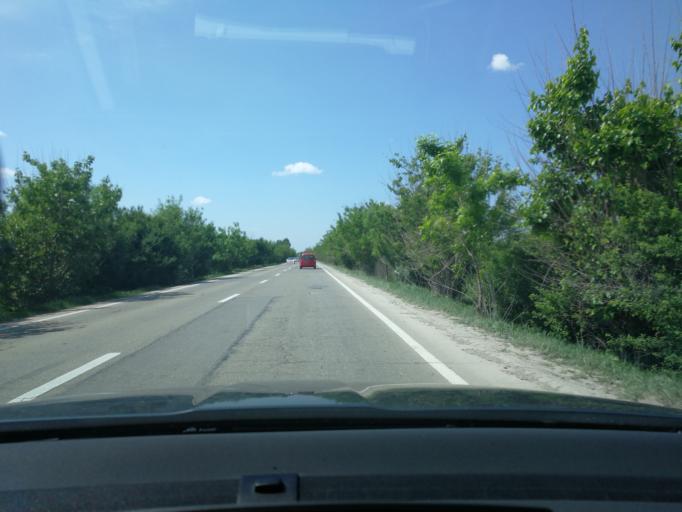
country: RO
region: Prahova
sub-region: Comuna Targsoru Vechi
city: Targsoru Vechi
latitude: 44.8789
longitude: 25.9447
